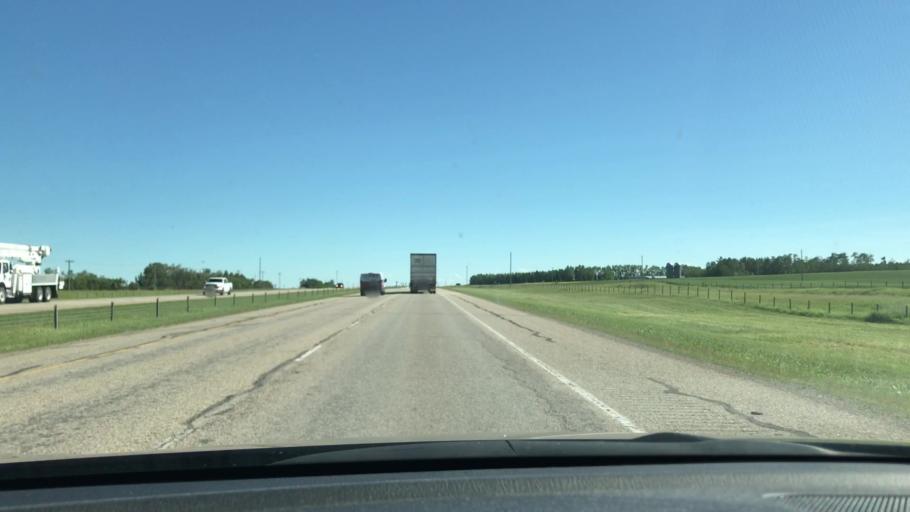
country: CA
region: Alberta
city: Olds
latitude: 51.8875
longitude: -114.0256
